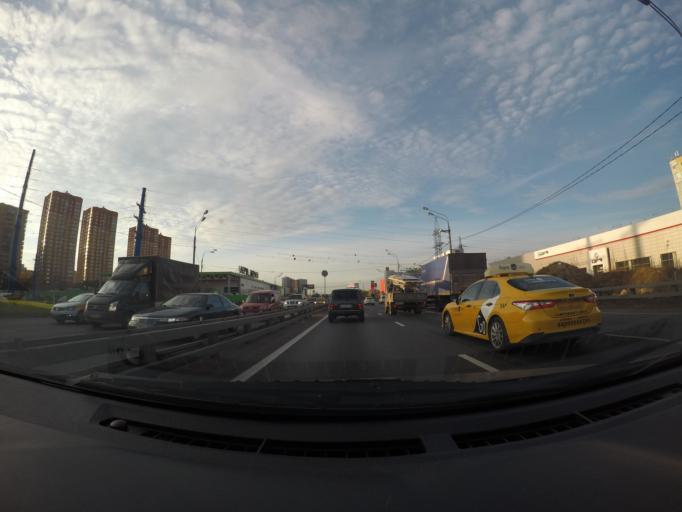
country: RU
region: Moscow
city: Khimki
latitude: 55.9024
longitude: 37.4194
